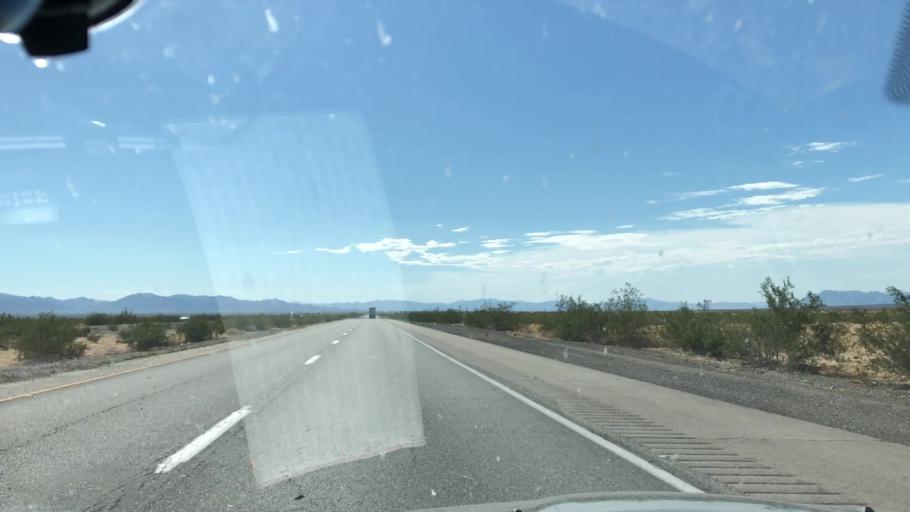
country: US
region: California
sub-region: Riverside County
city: Mesa Verde
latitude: 33.6264
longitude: -115.0565
